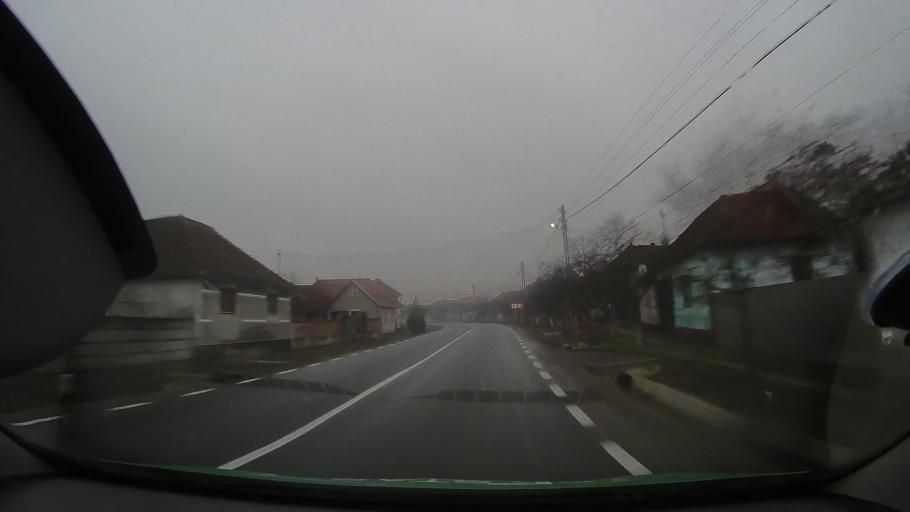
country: RO
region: Bihor
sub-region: Comuna Olcea
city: Calacea
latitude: 46.6430
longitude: 21.9558
